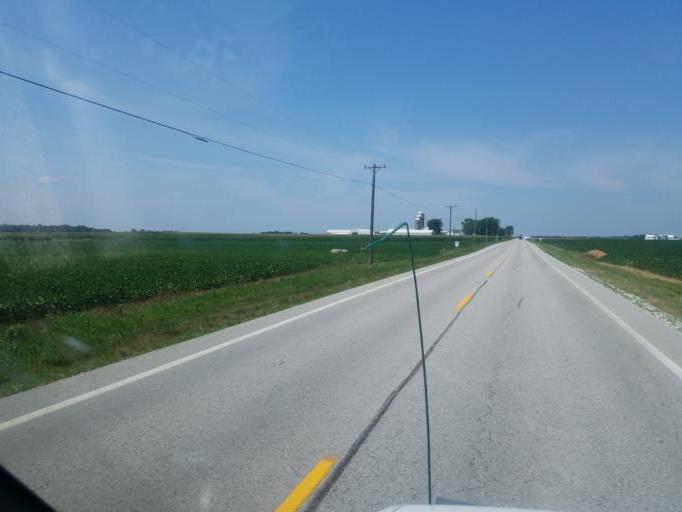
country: US
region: Ohio
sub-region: Auglaize County
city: New Bremen
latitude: 40.4528
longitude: -84.4341
